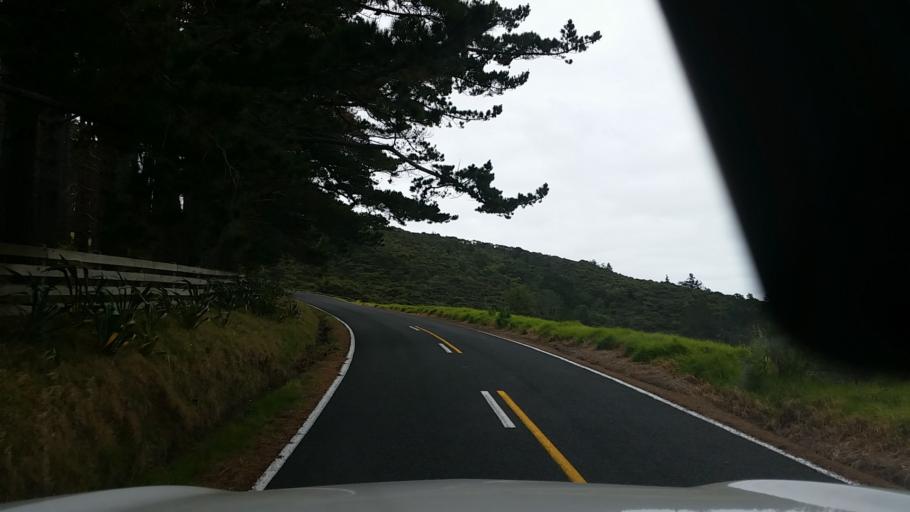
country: NZ
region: Auckland
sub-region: Auckland
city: Muriwai Beach
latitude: -36.8724
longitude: 174.4634
